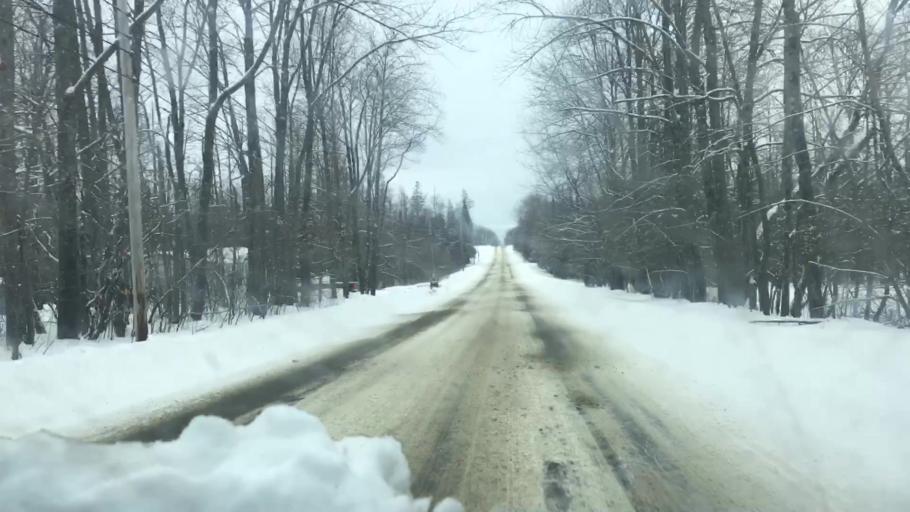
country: US
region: Maine
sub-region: Penobscot County
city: Bradford
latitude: 45.0117
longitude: -68.9935
